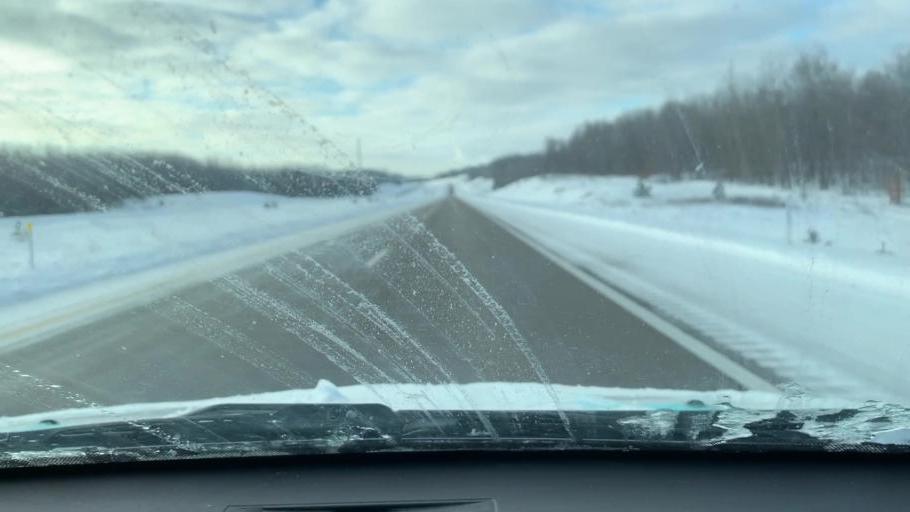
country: US
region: Michigan
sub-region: Wexford County
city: Manton
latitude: 44.3460
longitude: -85.4051
